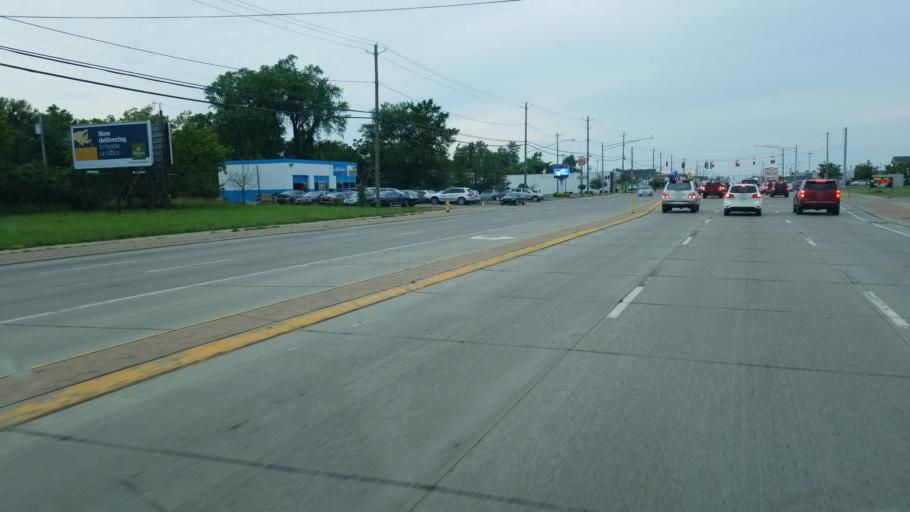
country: US
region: New York
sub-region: Erie County
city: Harris Hill
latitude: 42.9599
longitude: -78.6968
